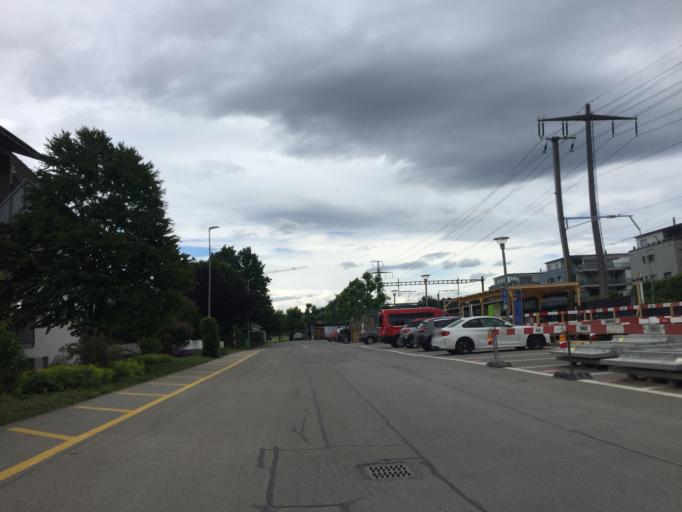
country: CH
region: Bern
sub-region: Bern-Mittelland District
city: Rubigen
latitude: 46.8981
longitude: 7.5458
